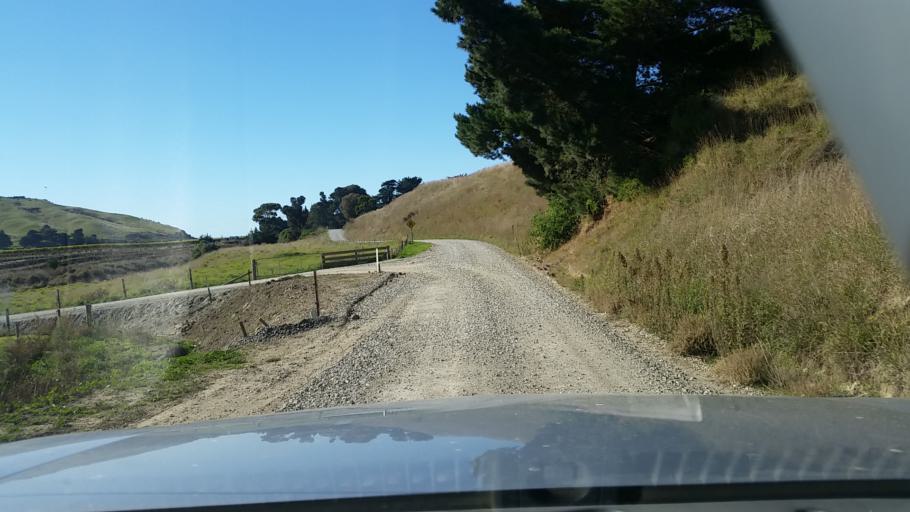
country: NZ
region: Marlborough
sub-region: Marlborough District
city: Blenheim
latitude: -41.6685
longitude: 174.1493
